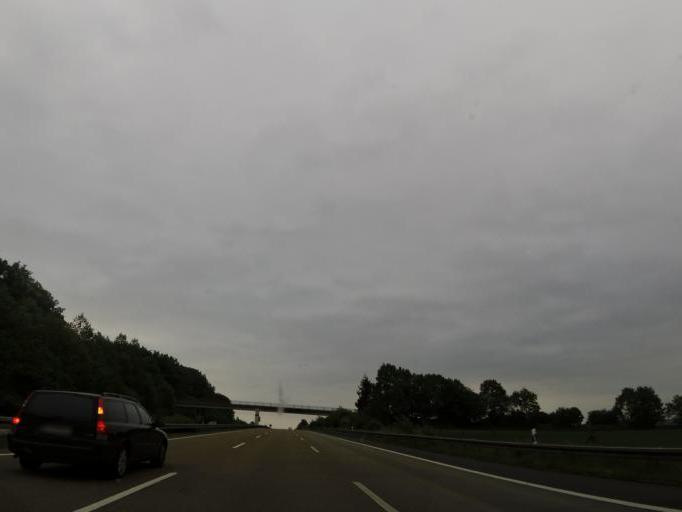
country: DE
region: Hesse
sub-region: Regierungsbezirk Kassel
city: Malsfeld
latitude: 51.0716
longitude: 9.4907
